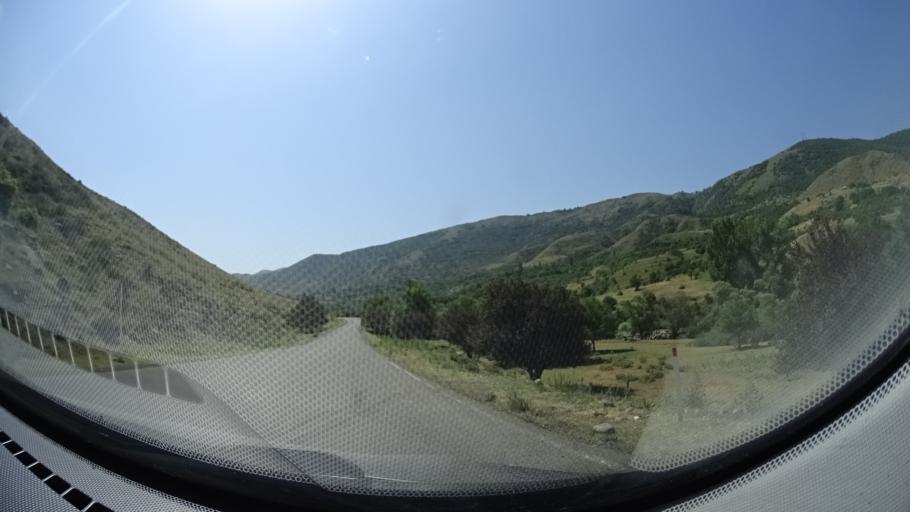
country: GE
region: Samtskhe-Javakheti
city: Aspindza
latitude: 41.6000
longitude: 43.1513
